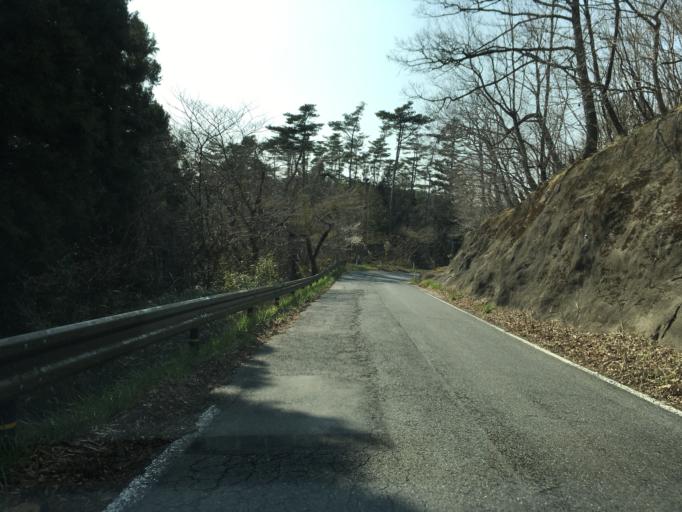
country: JP
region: Iwate
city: Ichinoseki
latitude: 38.8193
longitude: 141.3185
